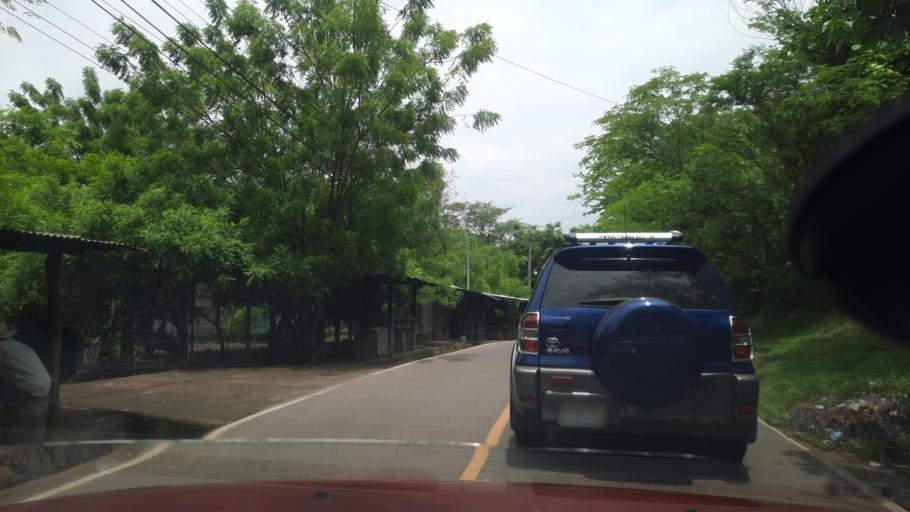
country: SV
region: La Union
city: Santa Rosa de Lima
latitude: 13.6481
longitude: -87.8507
